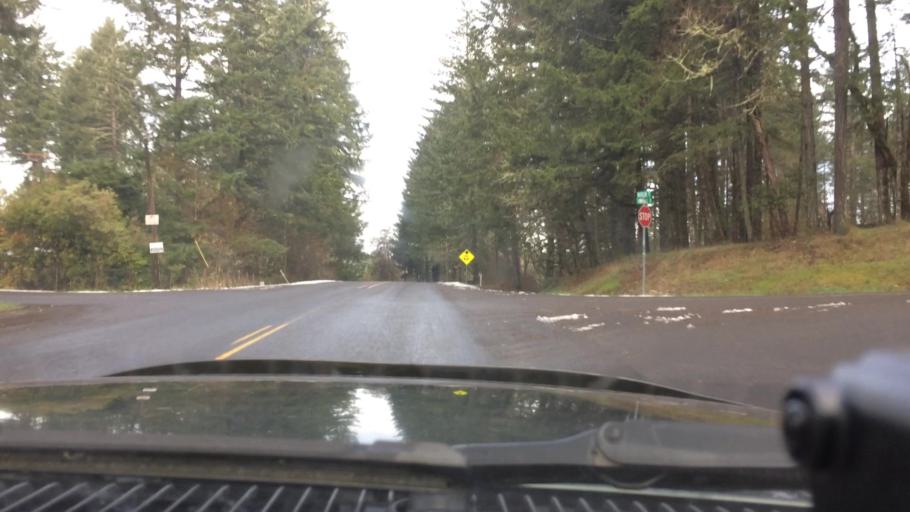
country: US
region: Oregon
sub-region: Lane County
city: Veneta
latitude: 44.1367
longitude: -123.3542
